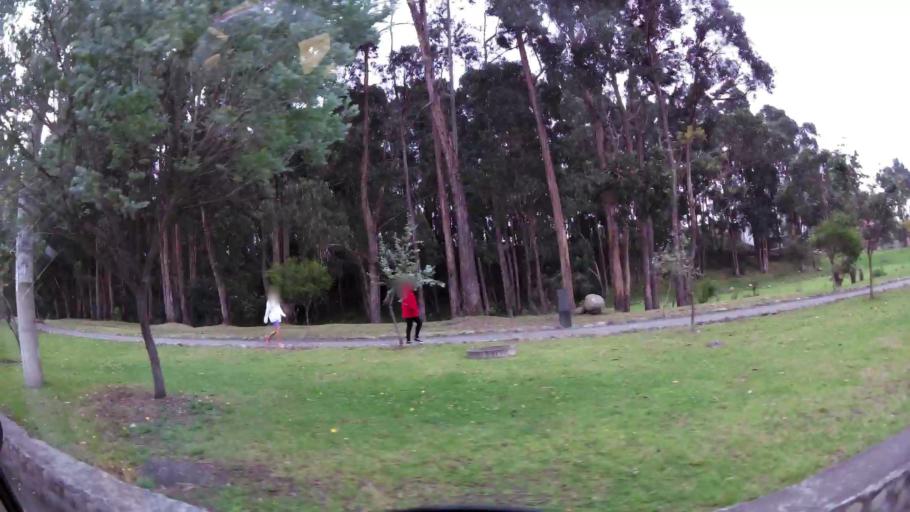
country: EC
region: Azuay
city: Cuenca
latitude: -2.9106
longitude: -79.0160
